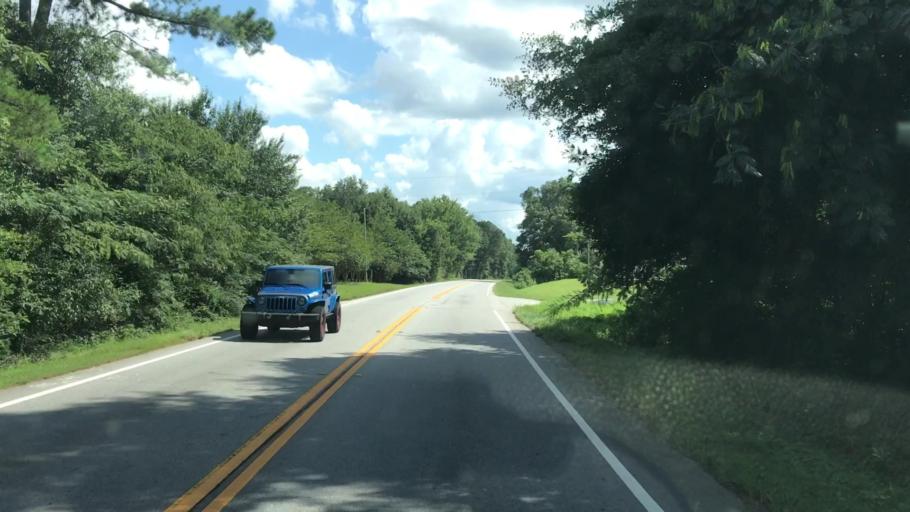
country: US
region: Georgia
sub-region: Newton County
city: Oxford
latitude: 33.6727
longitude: -83.8506
